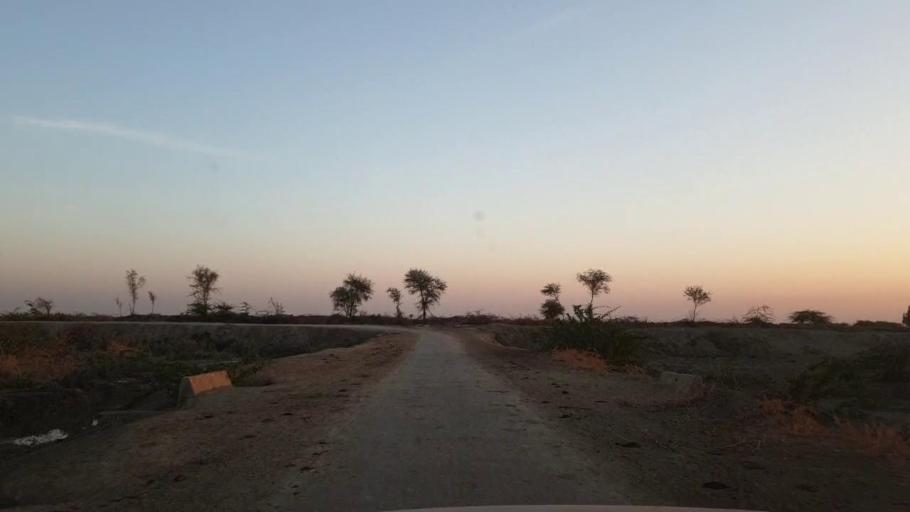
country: PK
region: Sindh
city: Samaro
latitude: 25.1489
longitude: 69.4257
